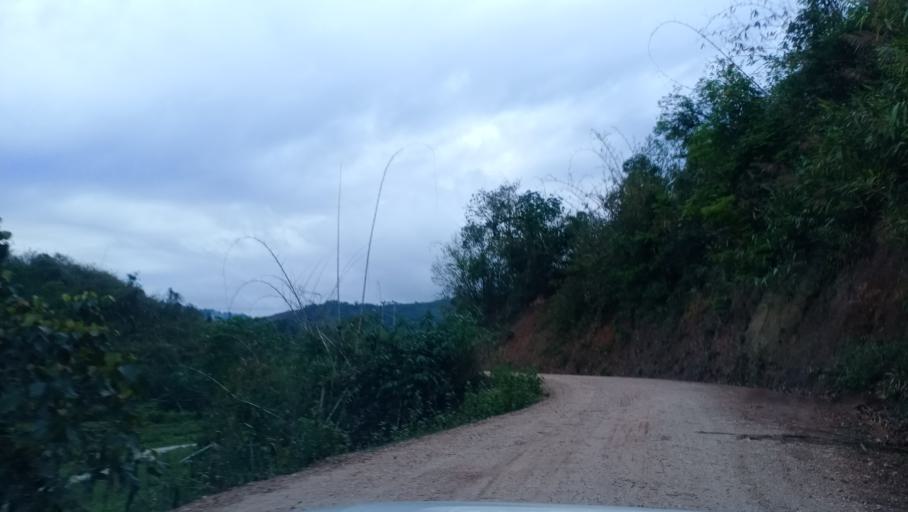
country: LA
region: Phongsali
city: Khoa
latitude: 21.2085
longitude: 102.6843
